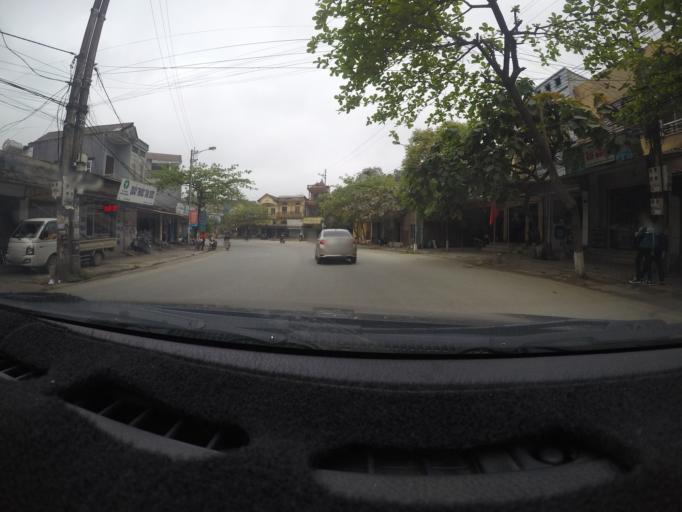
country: VN
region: Yen Bai
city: Yen Bai
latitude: 21.7325
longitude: 104.9593
